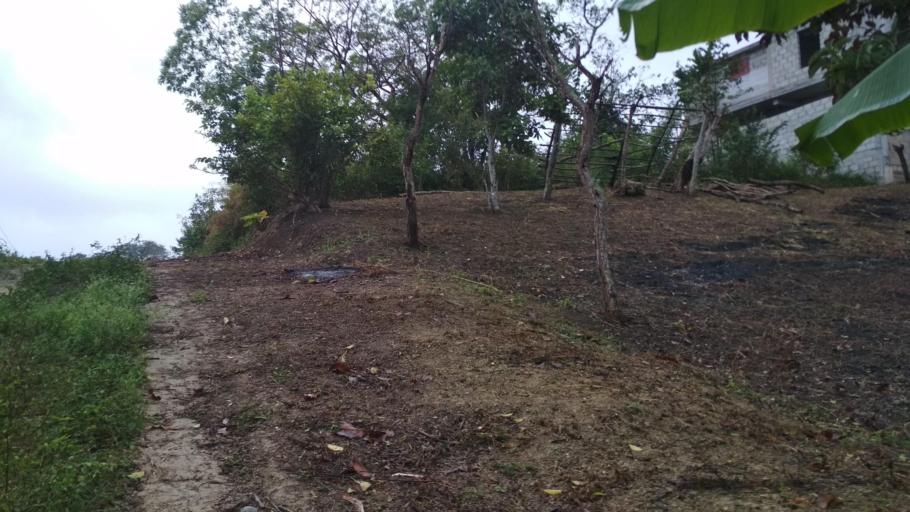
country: MX
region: Veracruz
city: Papantla de Olarte
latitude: 20.4659
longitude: -97.3096
